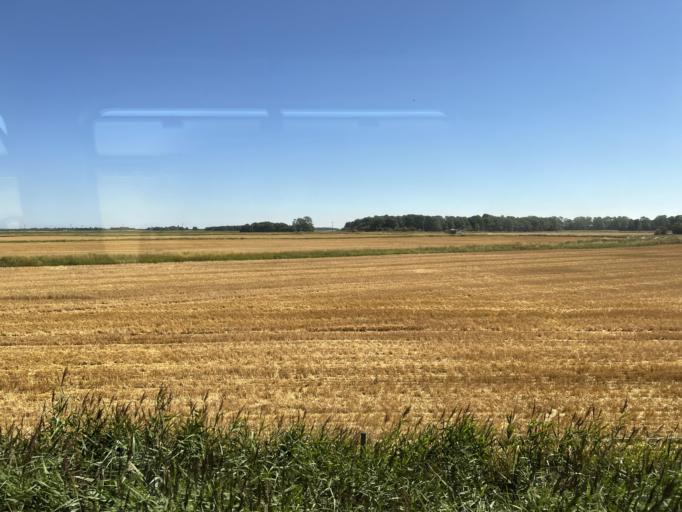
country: GB
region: England
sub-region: Lincolnshire
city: Spilsby
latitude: 53.1162
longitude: 0.1311
